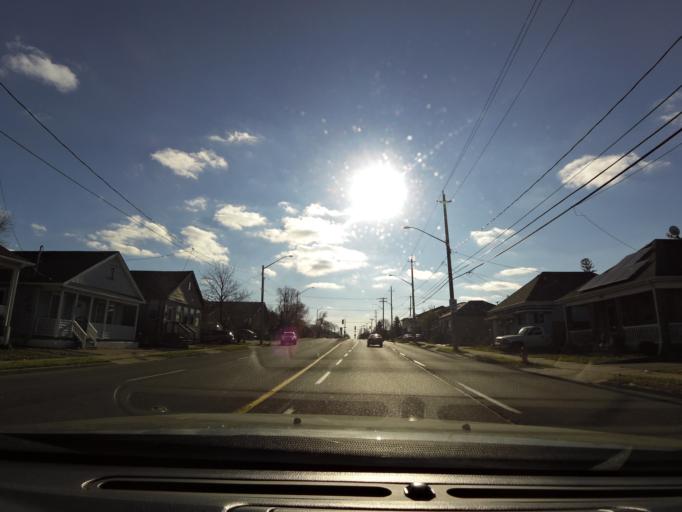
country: CA
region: Ontario
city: Hamilton
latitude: 43.2363
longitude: -79.8677
